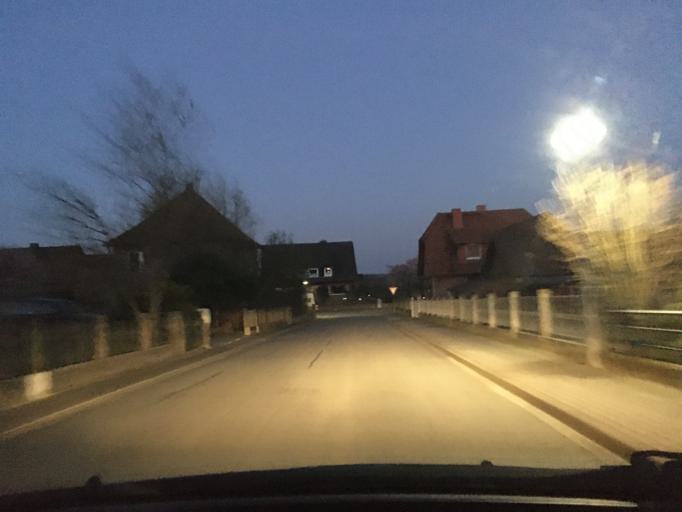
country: DE
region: Lower Saxony
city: Amelinghausen
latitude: 53.1215
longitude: 10.2089
